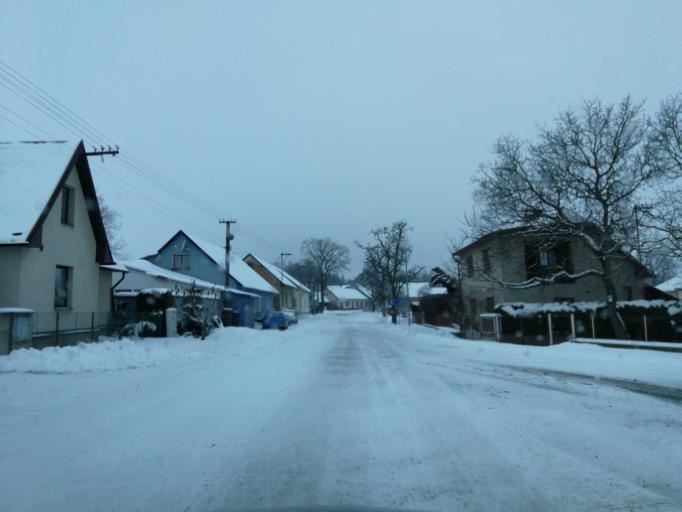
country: CZ
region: Vysocina
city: Heralec
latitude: 49.5294
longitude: 15.4614
